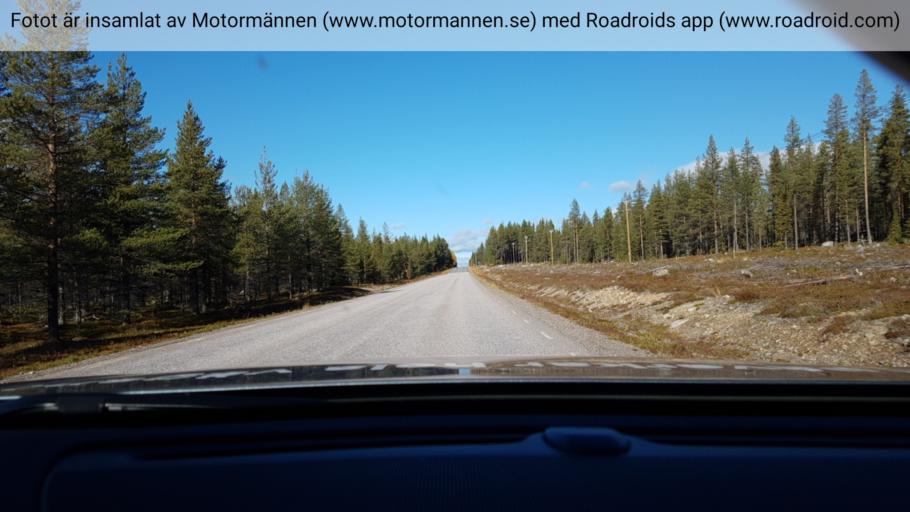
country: SE
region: Vaesterbotten
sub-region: Mala Kommun
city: Mala
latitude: 65.7834
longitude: 18.4991
